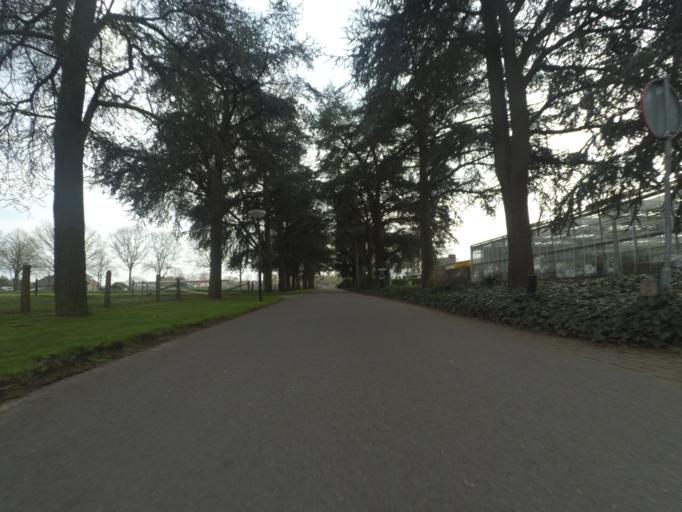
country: NL
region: Gelderland
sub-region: Gemeente Apeldoorn
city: Beekbergen
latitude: 52.1630
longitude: 5.9732
